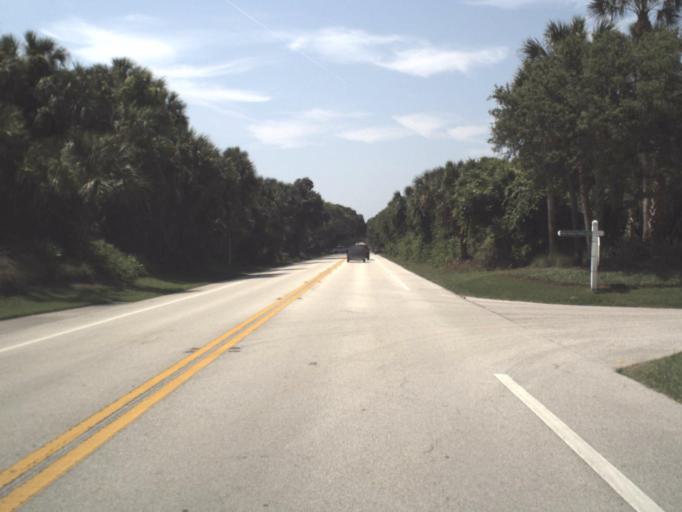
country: US
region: Florida
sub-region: Saint Johns County
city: Palm Valley
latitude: 30.1410
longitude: -81.3519
